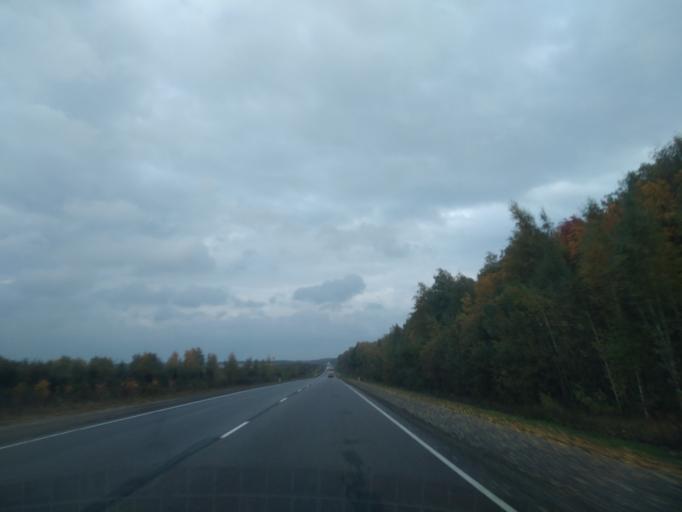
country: RU
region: Lipetsk
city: Donskoye
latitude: 52.5719
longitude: 39.1721
